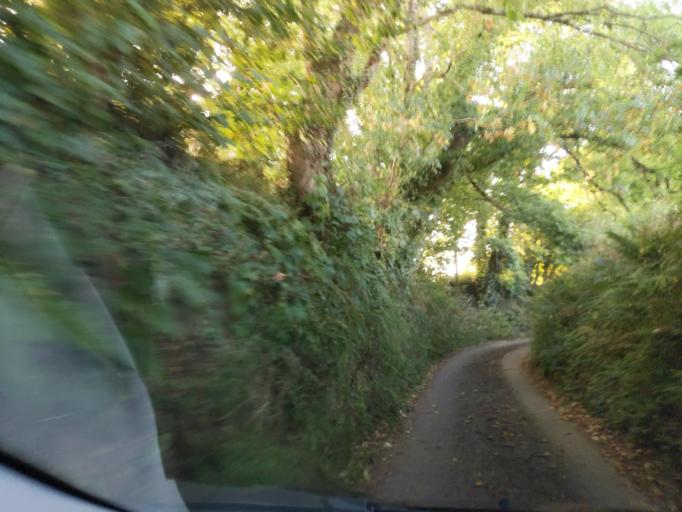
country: GB
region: England
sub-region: Cornwall
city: Fowey
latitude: 50.3675
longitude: -4.5928
